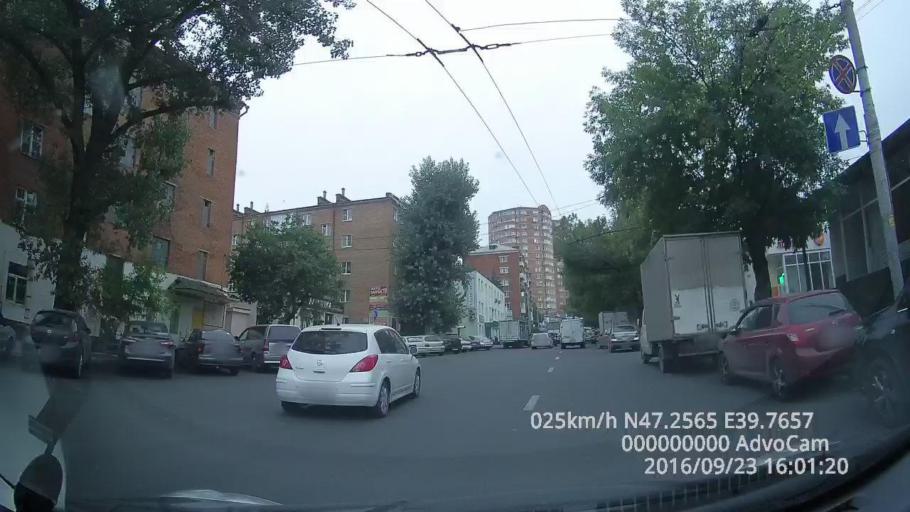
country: RU
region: Rostov
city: Imeni Chkalova
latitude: 47.2563
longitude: 39.7658
